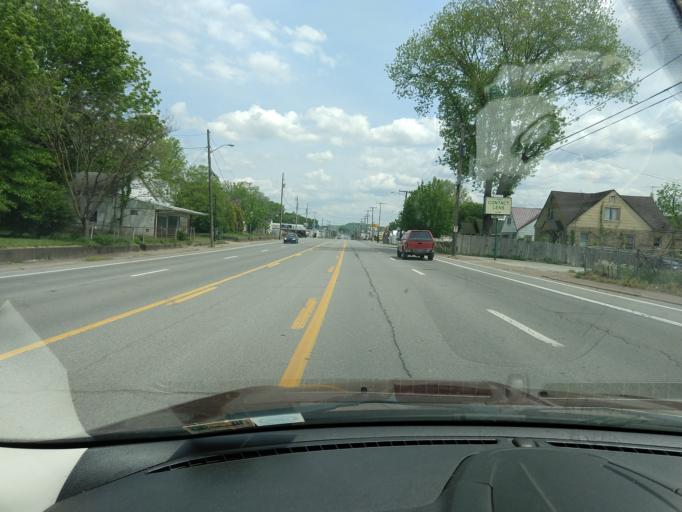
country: US
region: West Virginia
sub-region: Kanawha County
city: Dunbar
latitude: 38.3539
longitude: -81.7451
